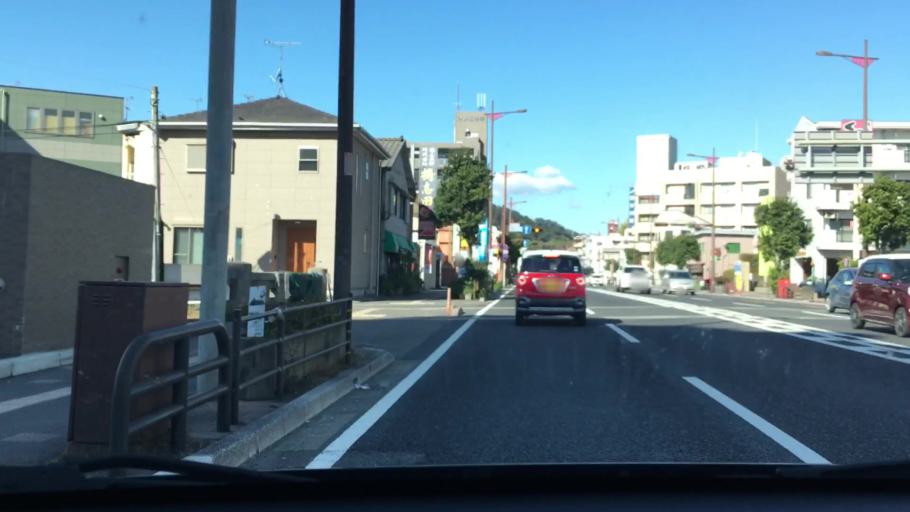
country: JP
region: Kagoshima
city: Kagoshima-shi
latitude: 31.6153
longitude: 130.5296
